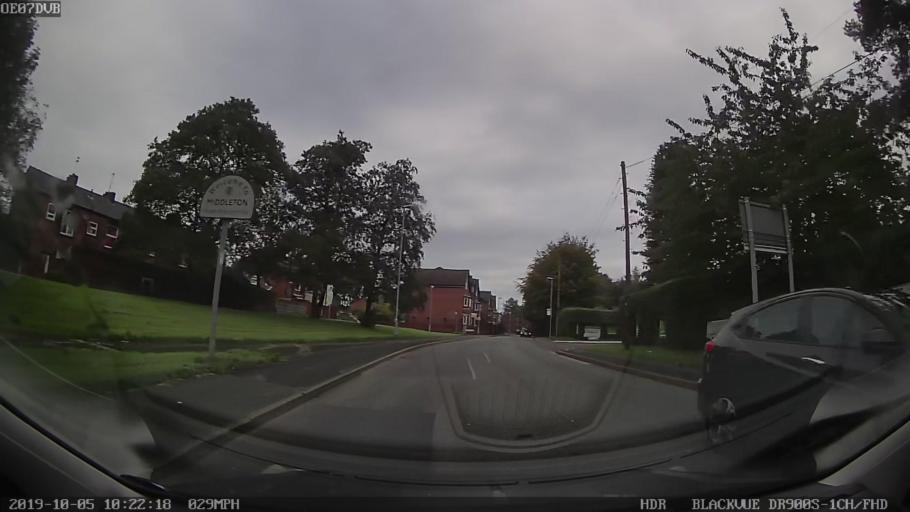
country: GB
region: England
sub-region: Borough of Rochdale
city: Middleton
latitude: 53.5429
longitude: -2.1721
